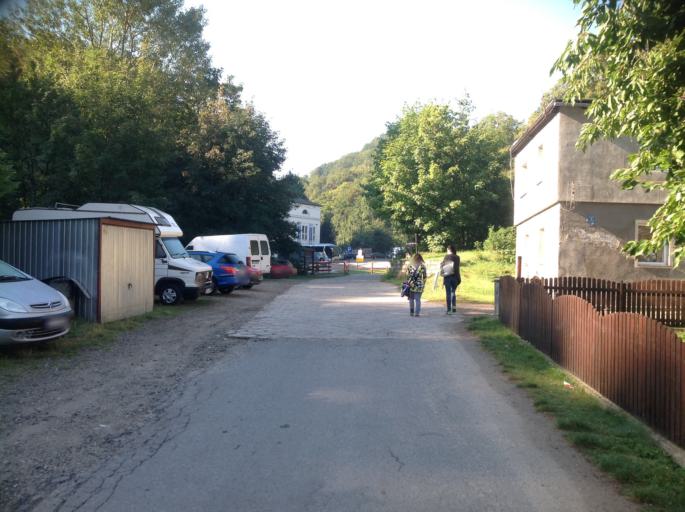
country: PL
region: Lower Silesian Voivodeship
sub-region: Powiat zabkowicki
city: Zloty Stok
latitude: 50.4421
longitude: 16.8766
